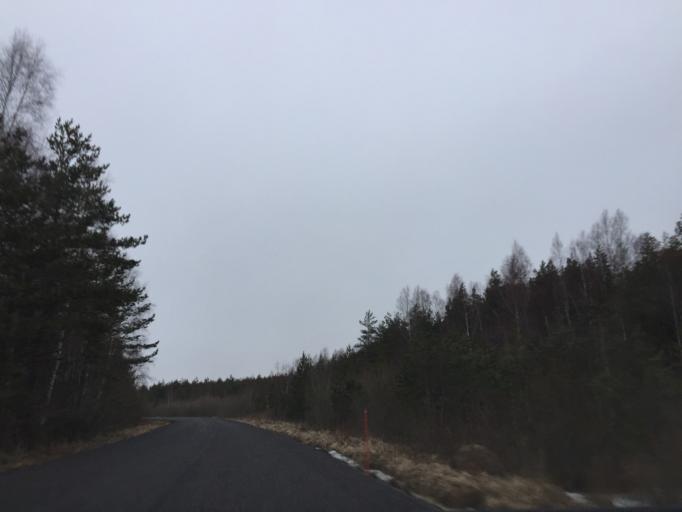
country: EE
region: Laeaene
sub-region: Ridala Parish
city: Uuemoisa
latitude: 58.6706
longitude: 23.5623
